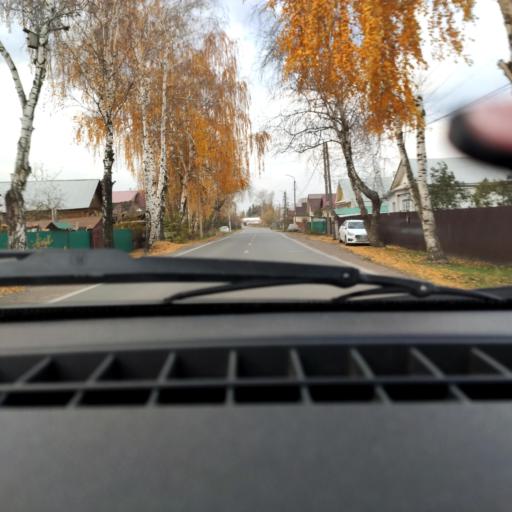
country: RU
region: Bashkortostan
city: Iglino
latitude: 54.8297
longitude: 56.1884
